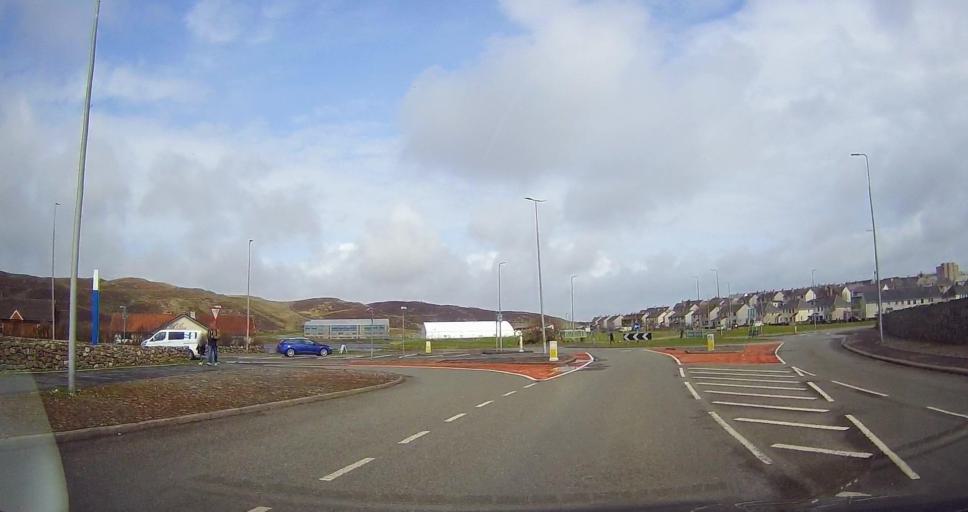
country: GB
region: Scotland
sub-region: Shetland Islands
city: Lerwick
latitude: 60.1484
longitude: -1.1599
